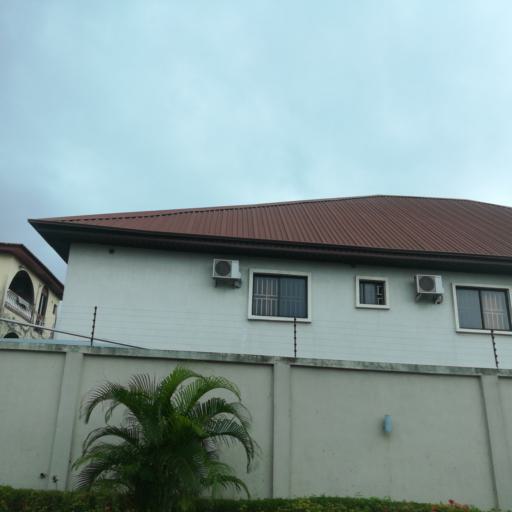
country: NG
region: Lagos
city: Ikoyi
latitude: 6.4397
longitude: 3.4628
